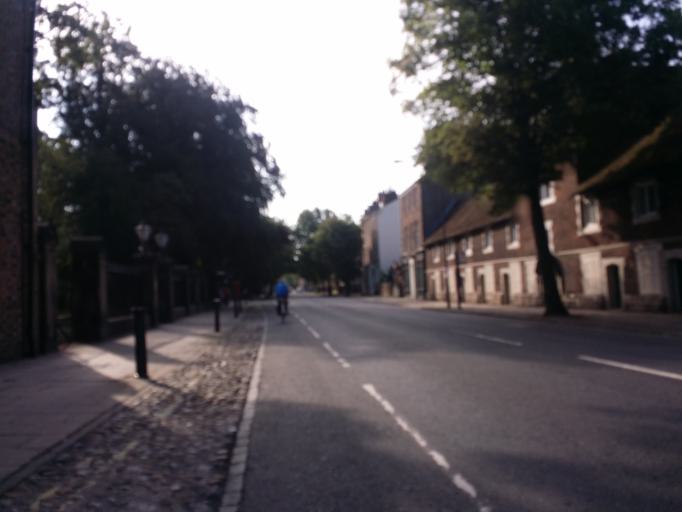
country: GB
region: England
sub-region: City of York
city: York
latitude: 53.9657
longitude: -1.0904
